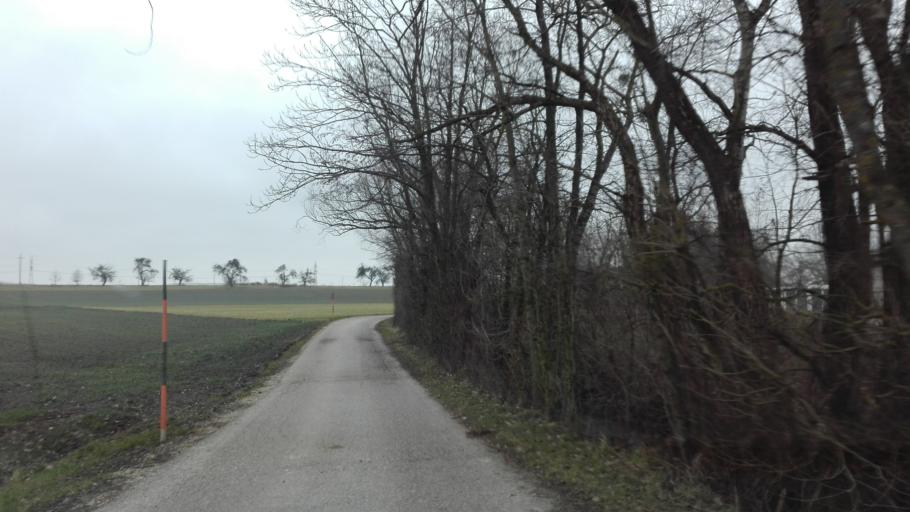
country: AT
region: Upper Austria
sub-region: Wels-Land
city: Marchtrenk
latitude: 48.2110
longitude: 14.1399
